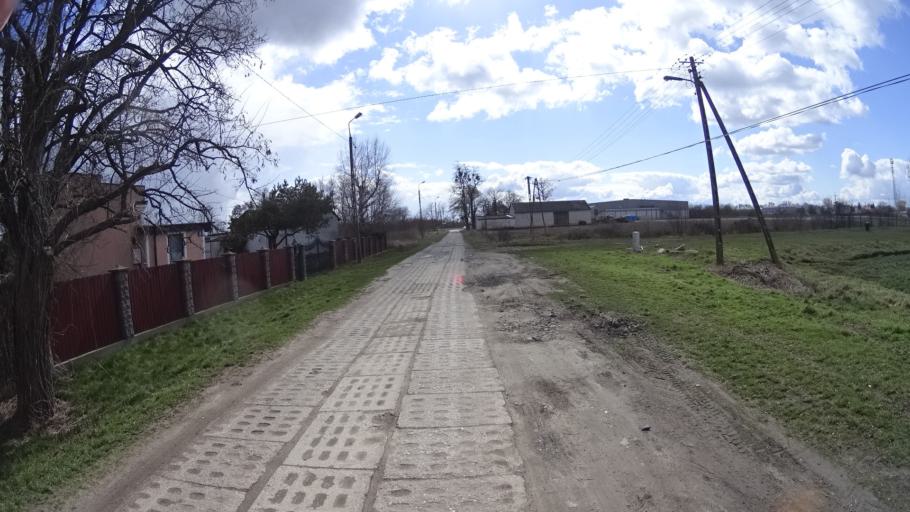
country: PL
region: Masovian Voivodeship
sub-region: Powiat warszawski zachodni
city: Jozefow
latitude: 52.2167
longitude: 20.7151
